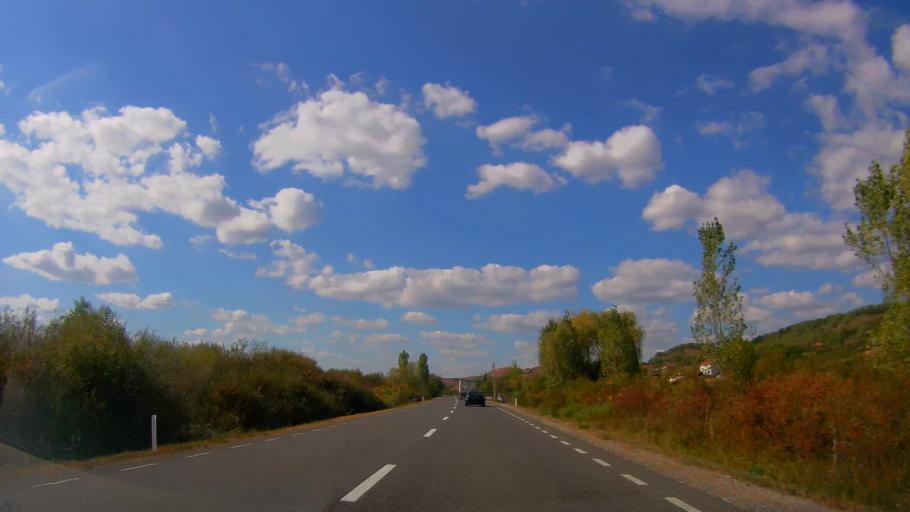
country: RO
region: Salaj
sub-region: Comuna Bocsa
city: Bocsa
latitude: 47.3148
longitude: 22.9109
